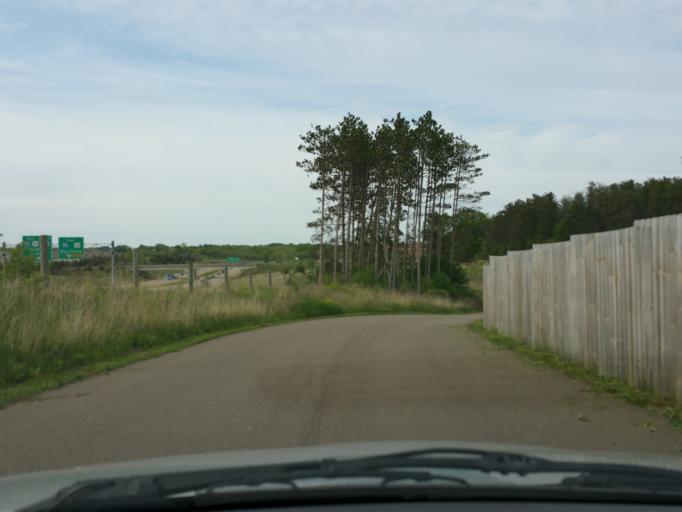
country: US
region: Wisconsin
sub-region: Saint Croix County
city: Hudson
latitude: 44.9551
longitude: -92.6942
